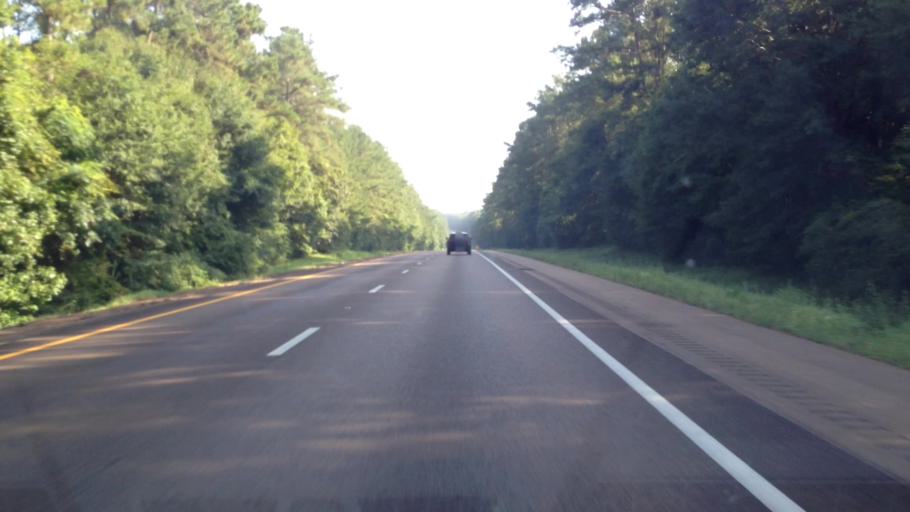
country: US
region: Mississippi
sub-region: Pike County
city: Summit
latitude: 31.3198
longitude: -90.4774
